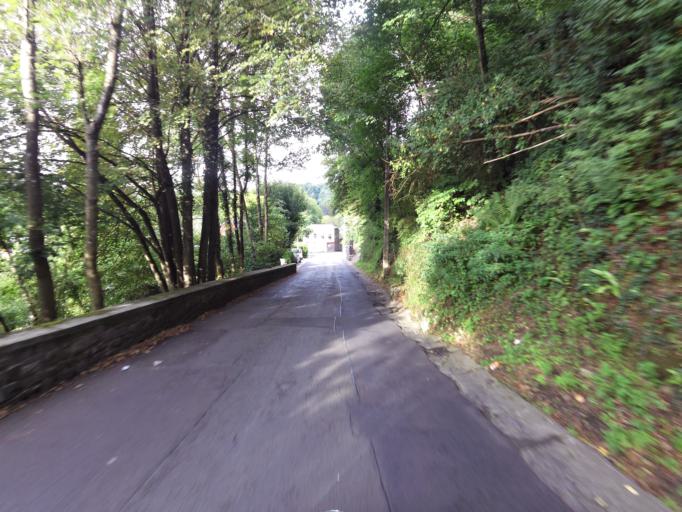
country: BE
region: Wallonia
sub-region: Province du Luxembourg
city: Durbuy
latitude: 50.3499
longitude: 5.4535
